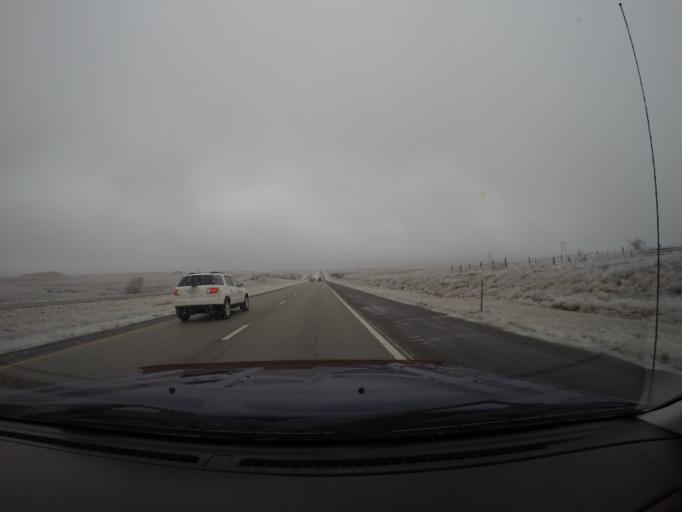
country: US
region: Kansas
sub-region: Riley County
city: Manhattan
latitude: 39.0780
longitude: -96.5382
